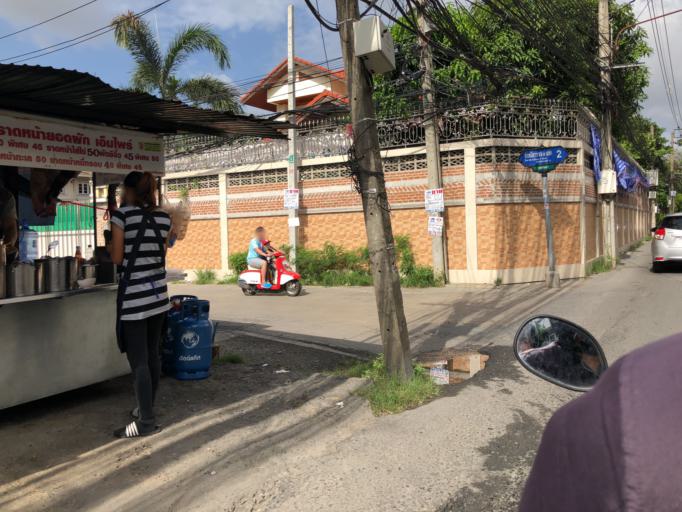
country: TH
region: Bangkok
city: Watthana
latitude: 13.7198
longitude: 100.5985
